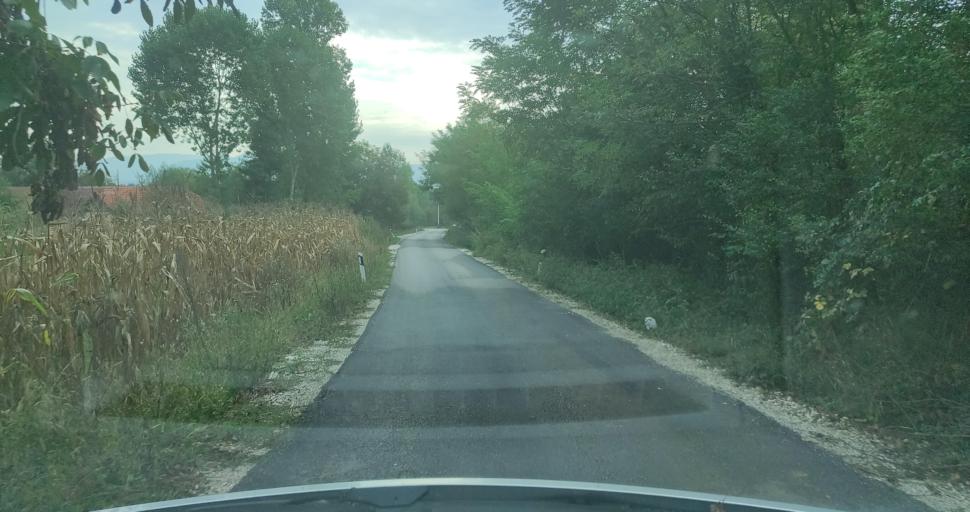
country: RS
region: Central Serbia
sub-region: Pcinjski Okrug
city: Vladicin Han
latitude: 42.6716
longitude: 22.0224
